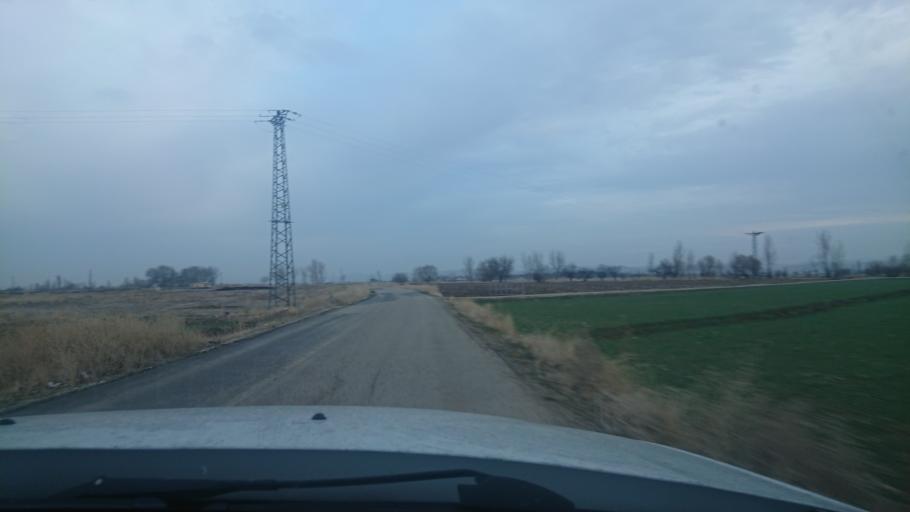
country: TR
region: Aksaray
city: Yesilova
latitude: 38.4436
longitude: 33.8370
